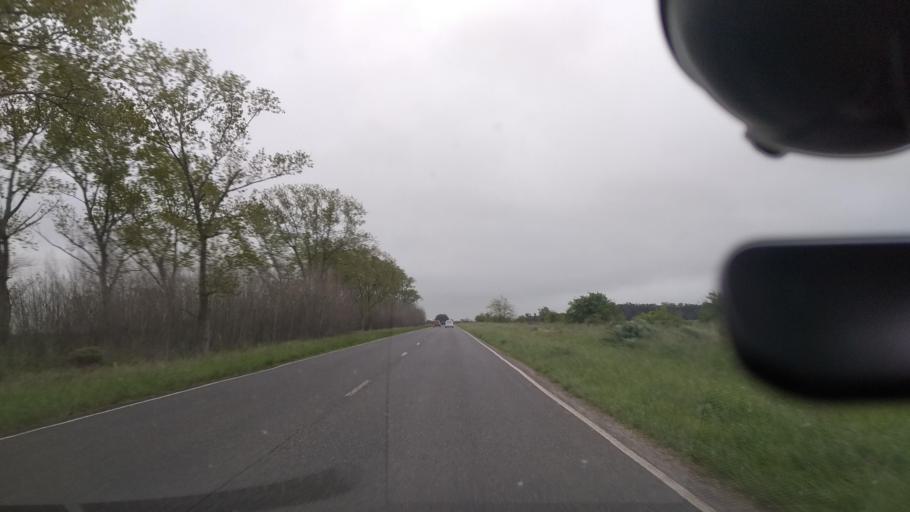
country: AR
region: Buenos Aires
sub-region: Partido de Magdalena
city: Magdalena
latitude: -35.2414
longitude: -57.6882
